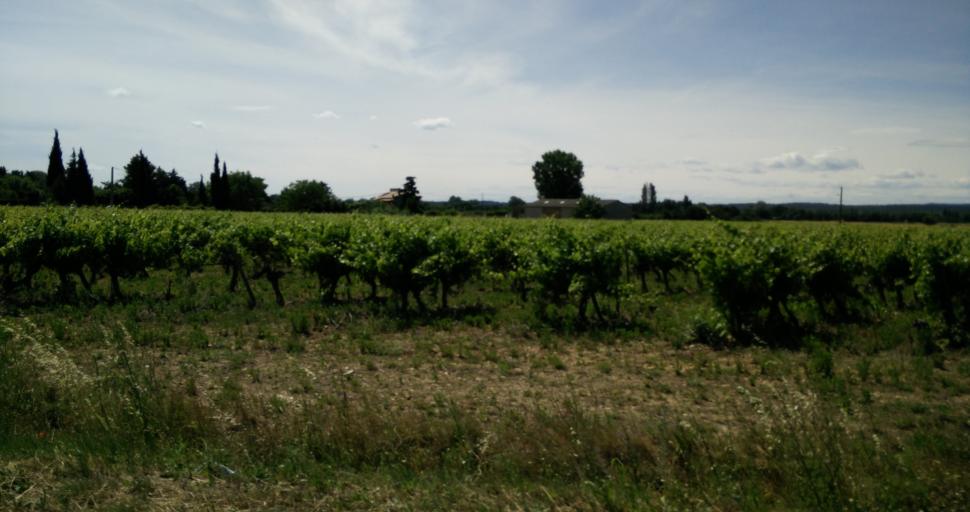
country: FR
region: Languedoc-Roussillon
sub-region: Departement du Gard
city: Aubord
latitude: 43.7553
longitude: 4.3094
